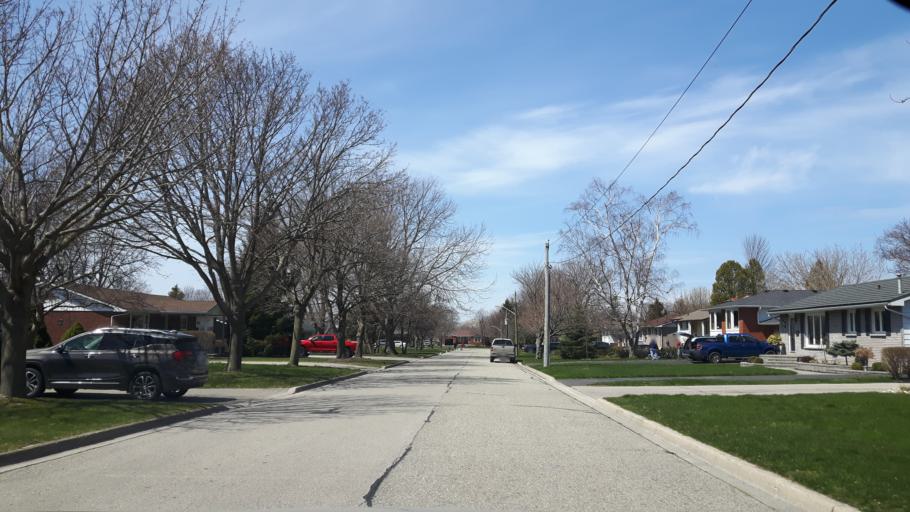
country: CA
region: Ontario
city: Goderich
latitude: 43.7327
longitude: -81.7189
